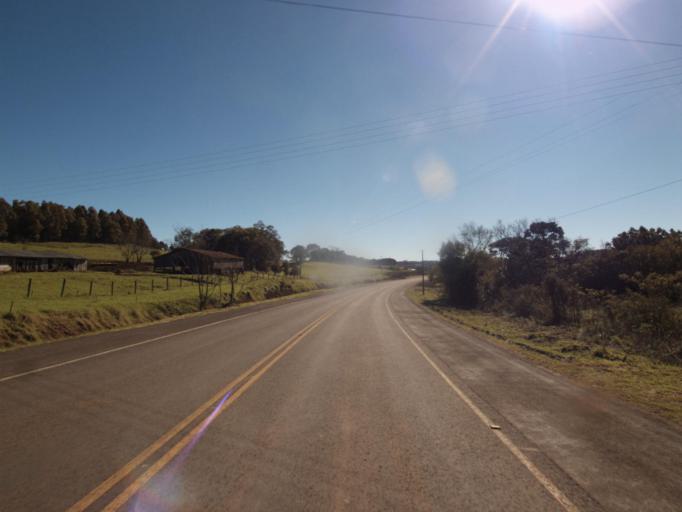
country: AR
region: Misiones
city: Bernardo de Irigoyen
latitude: -26.6386
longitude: -53.6332
